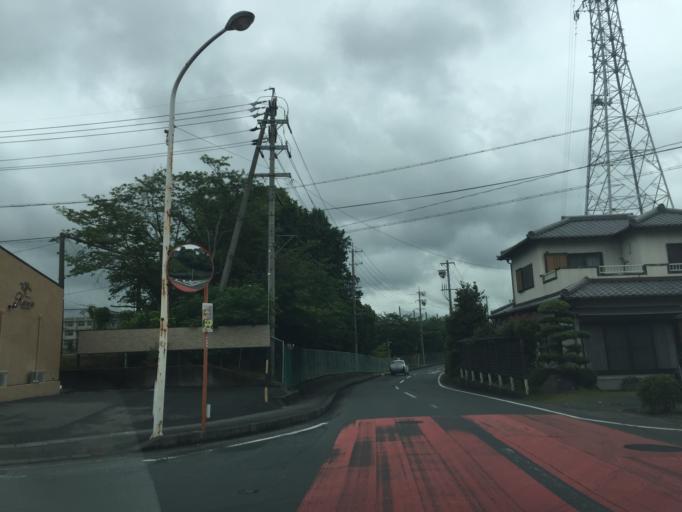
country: JP
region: Shizuoka
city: Fukuroi
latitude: 34.7641
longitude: 137.9168
